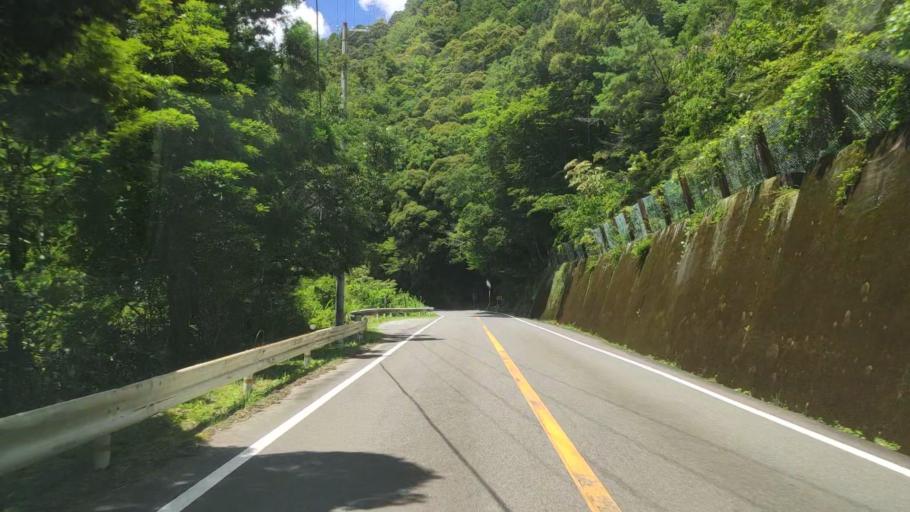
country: JP
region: Mie
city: Owase
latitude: 33.9978
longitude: 136.0219
